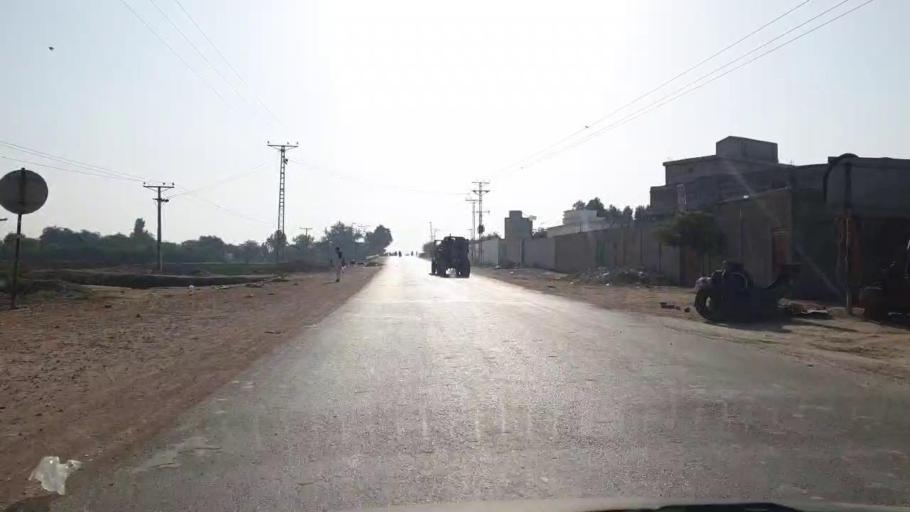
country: PK
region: Sindh
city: Badin
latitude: 24.6763
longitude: 68.8488
